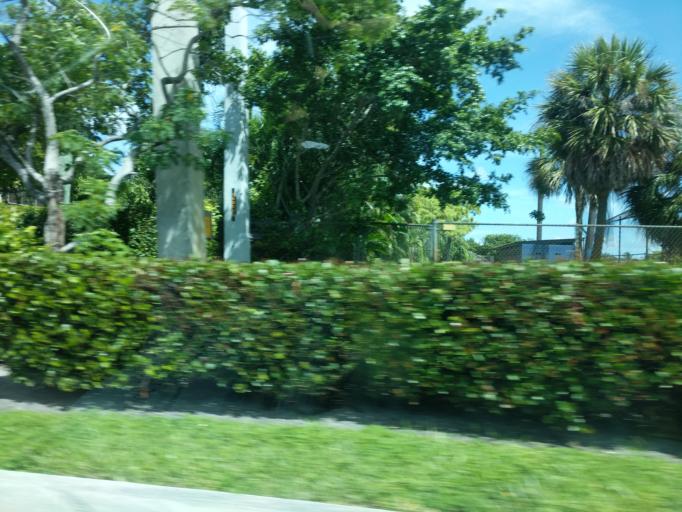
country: US
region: Florida
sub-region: Broward County
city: Deerfield Beach
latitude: 26.3050
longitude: -80.0985
